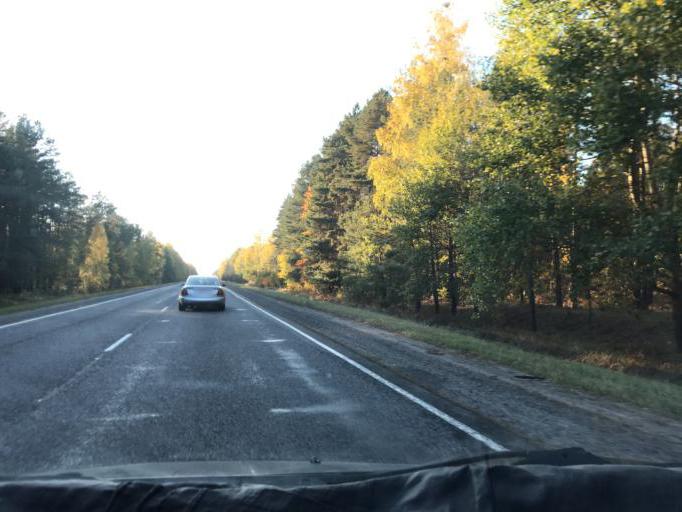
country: BY
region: Gomel
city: Zhytkavichy
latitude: 52.2726
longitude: 28.0728
